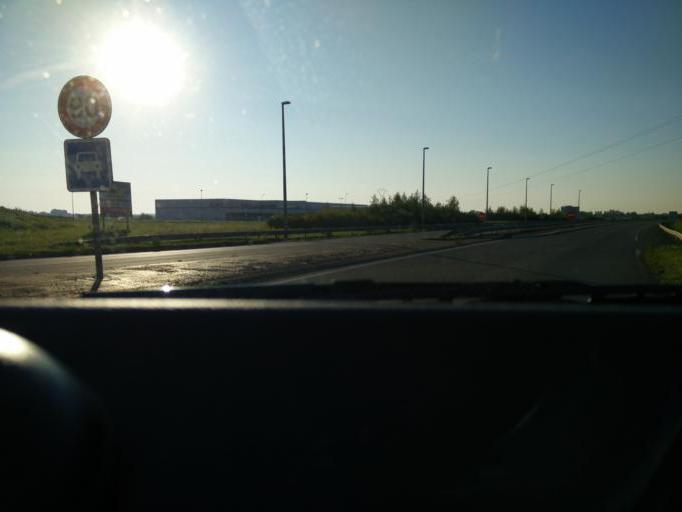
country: FR
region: Nord-Pas-de-Calais
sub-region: Departement du Nord
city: Illies
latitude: 50.5475
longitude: 2.8245
